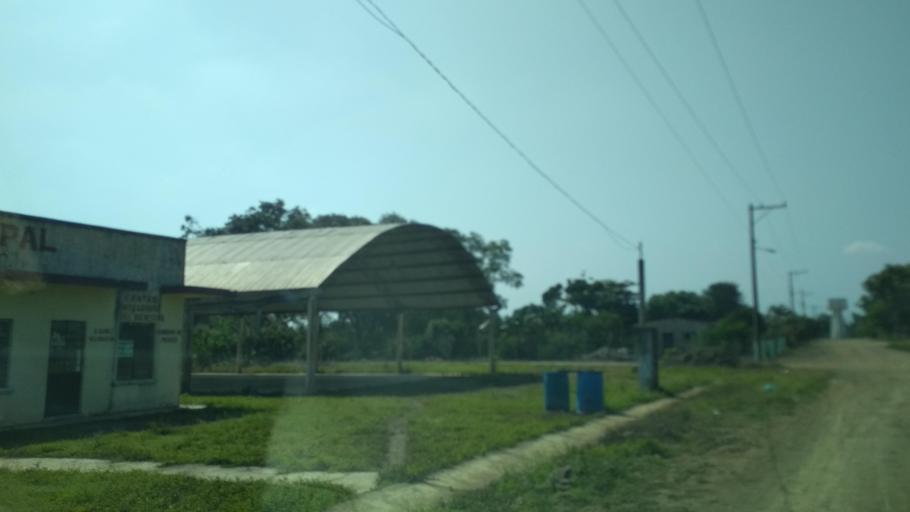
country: MX
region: Puebla
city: San Jose Acateno
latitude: 20.1945
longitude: -97.1862
